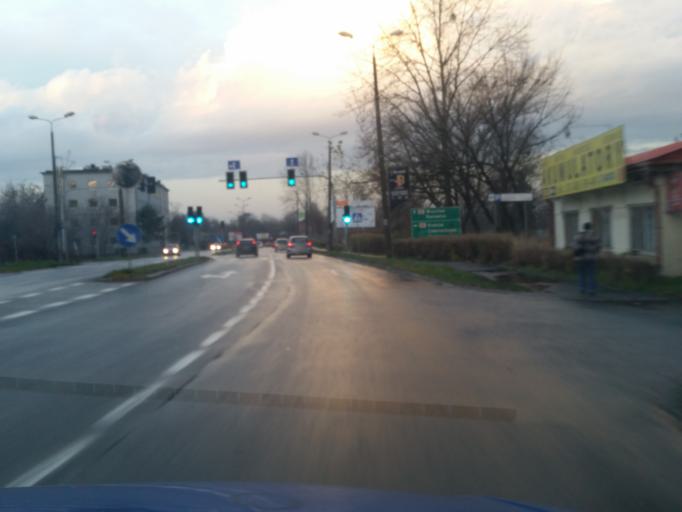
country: PL
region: Silesian Voivodeship
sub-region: Dabrowa Gornicza
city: Dabrowa Gornicza
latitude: 50.3137
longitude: 19.1954
